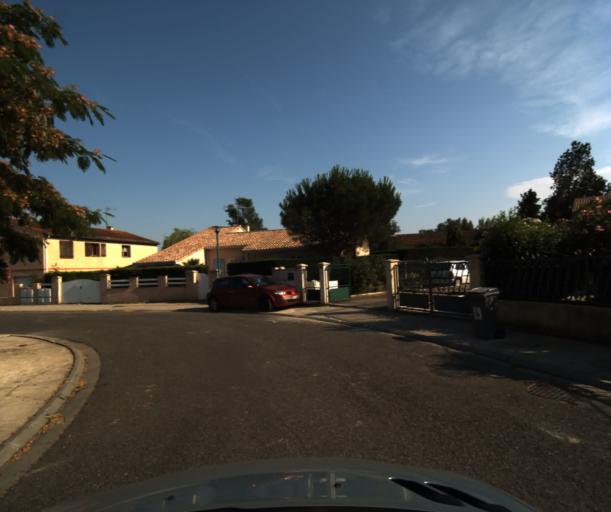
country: FR
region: Midi-Pyrenees
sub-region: Departement de la Haute-Garonne
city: Labarthe-sur-Leze
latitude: 43.4754
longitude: 1.3983
